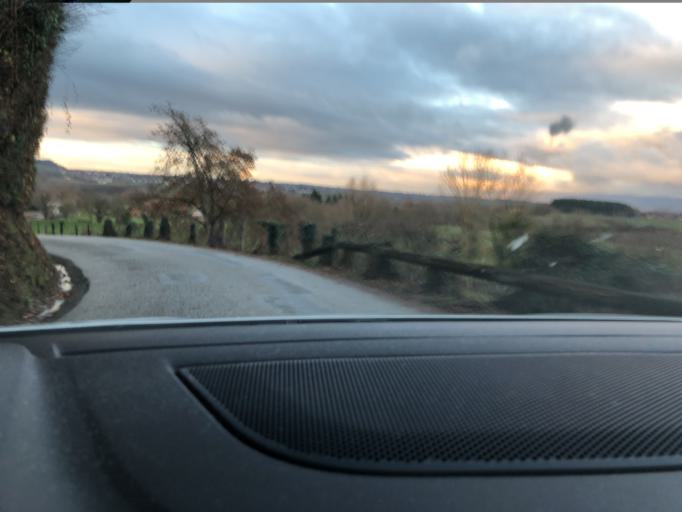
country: FR
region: Rhone-Alpes
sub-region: Departement de l'Isere
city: Fitilieu
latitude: 45.5235
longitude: 5.5566
